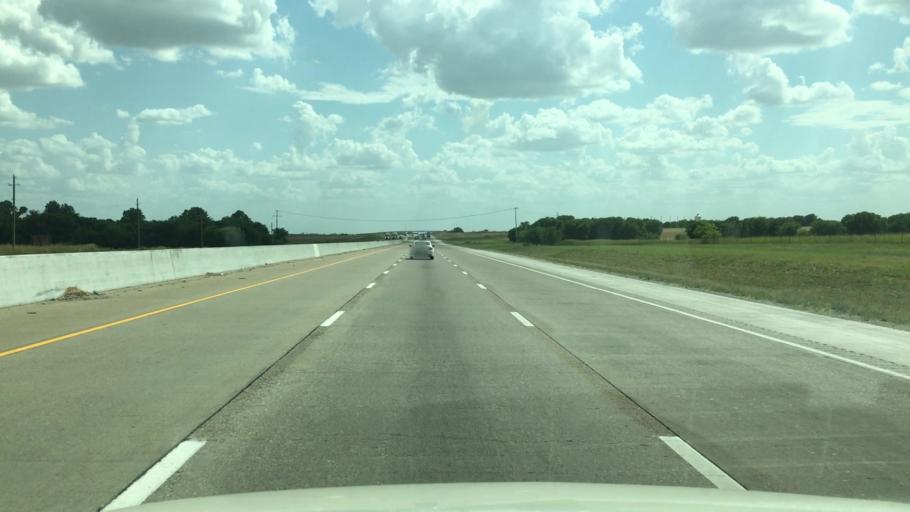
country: US
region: Texas
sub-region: Ellis County
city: Italy
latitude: 32.1610
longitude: -96.9227
